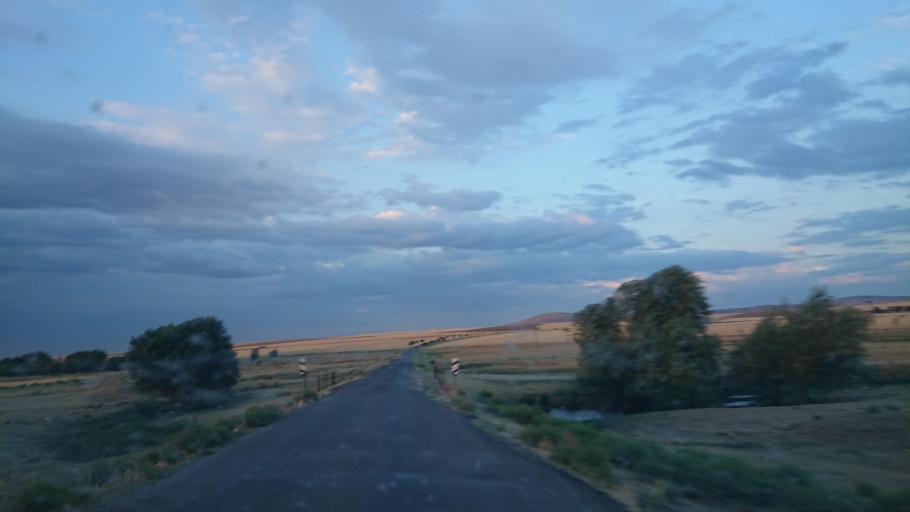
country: TR
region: Aksaray
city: Balci
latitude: 38.8272
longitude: 34.1286
